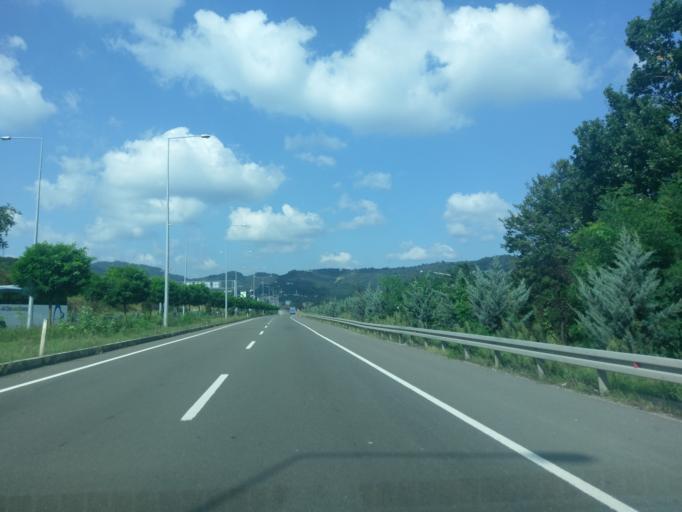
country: TR
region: Ordu
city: Unieh
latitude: 41.1148
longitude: 37.2768
